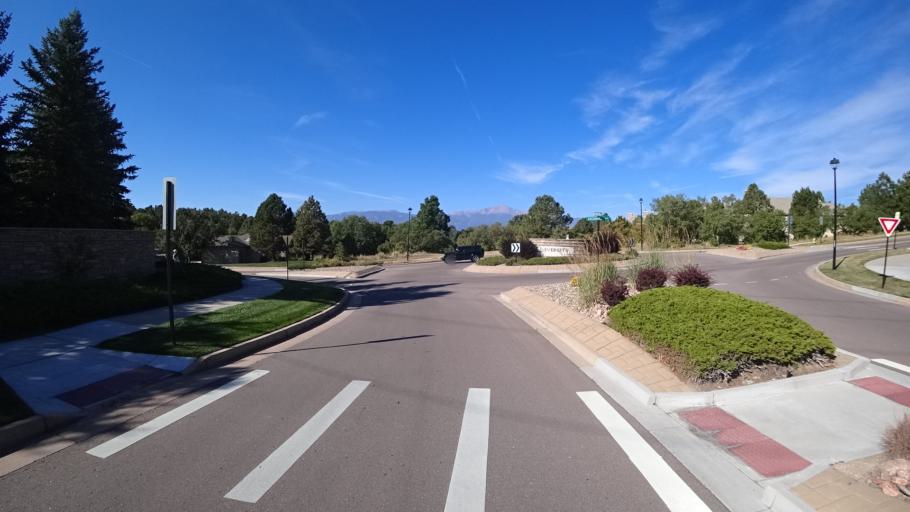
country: US
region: Colorado
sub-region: El Paso County
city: Colorado Springs
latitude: 38.9101
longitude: -104.7895
